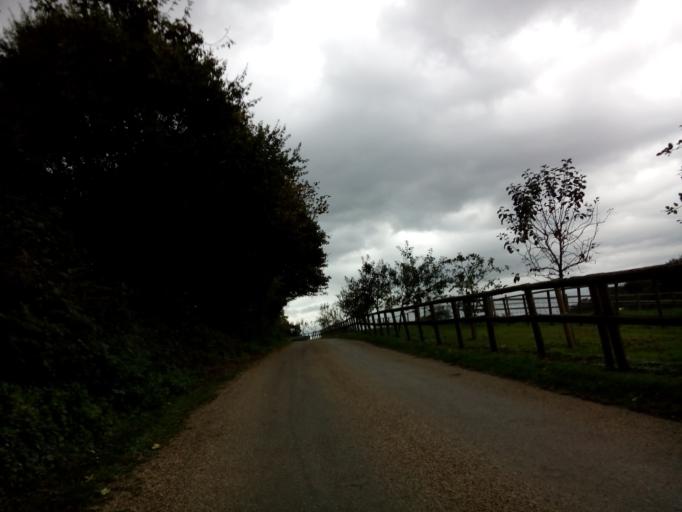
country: GB
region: England
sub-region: Suffolk
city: Ipswich
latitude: 52.0189
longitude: 1.1253
